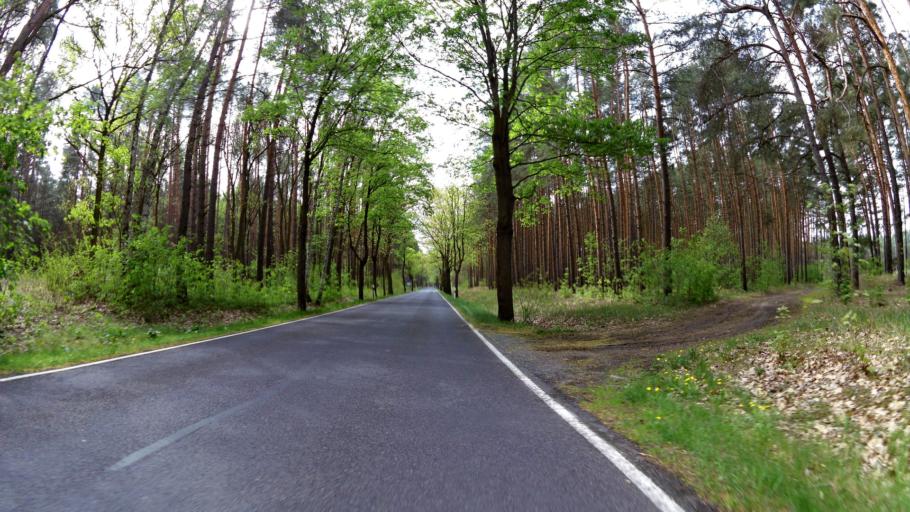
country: DE
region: Brandenburg
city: Bestensee
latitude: 52.2523
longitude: 13.7254
